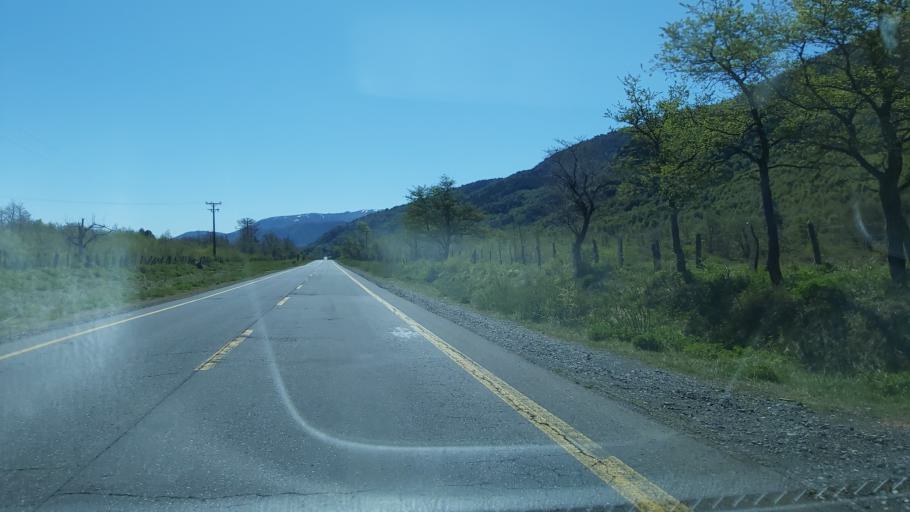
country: CL
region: Araucania
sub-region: Provincia de Cautin
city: Vilcun
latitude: -38.4767
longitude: -71.5438
